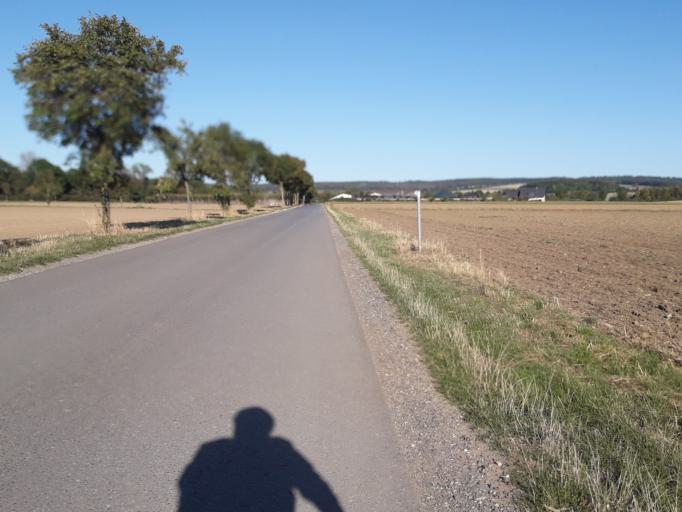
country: DE
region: North Rhine-Westphalia
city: Bad Lippspringe
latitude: 51.7548
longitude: 8.8146
